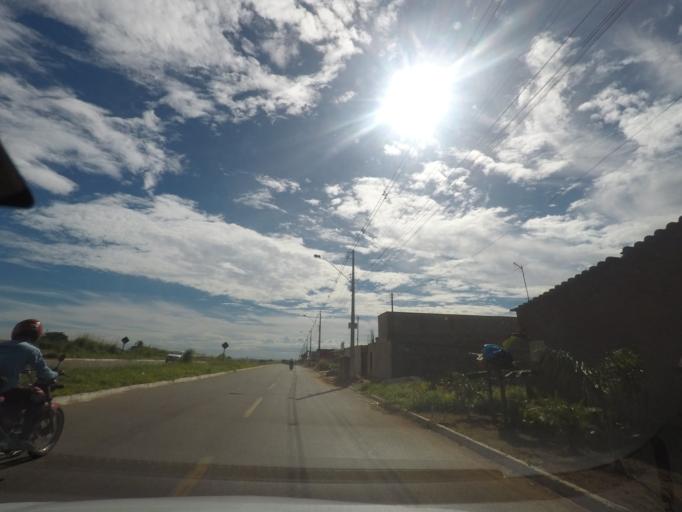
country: BR
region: Goias
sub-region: Aparecida De Goiania
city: Aparecida de Goiania
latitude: -16.8108
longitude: -49.2800
